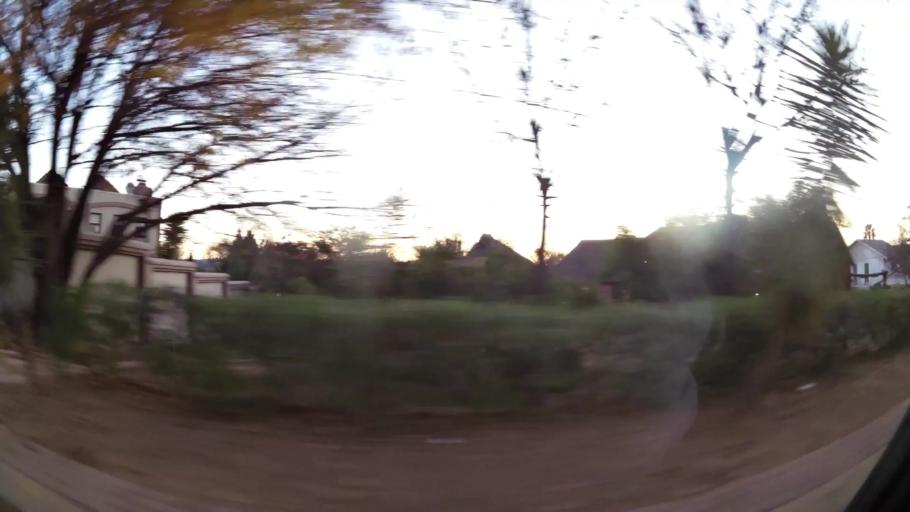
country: ZA
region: Gauteng
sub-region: City of Johannesburg Metropolitan Municipality
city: Diepsloot
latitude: -26.0389
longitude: 27.9892
